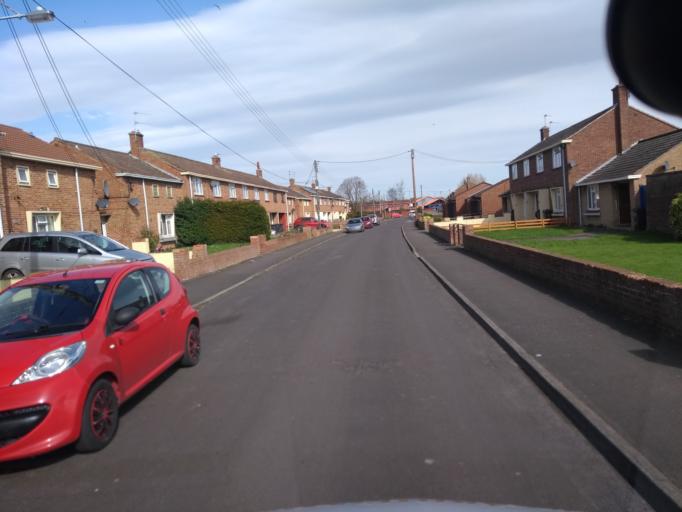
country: GB
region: England
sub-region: Somerset
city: Bridgwater
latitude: 51.1291
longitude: -2.9848
